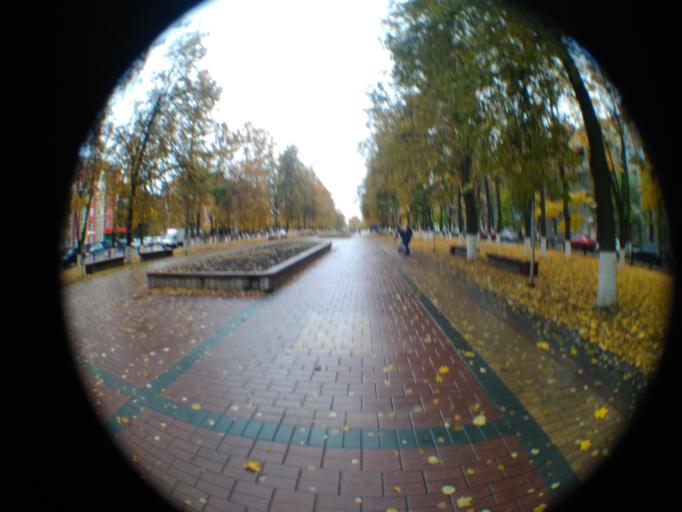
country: RU
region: Moskovskaya
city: Zhukovskiy
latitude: 55.5948
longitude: 38.1221
